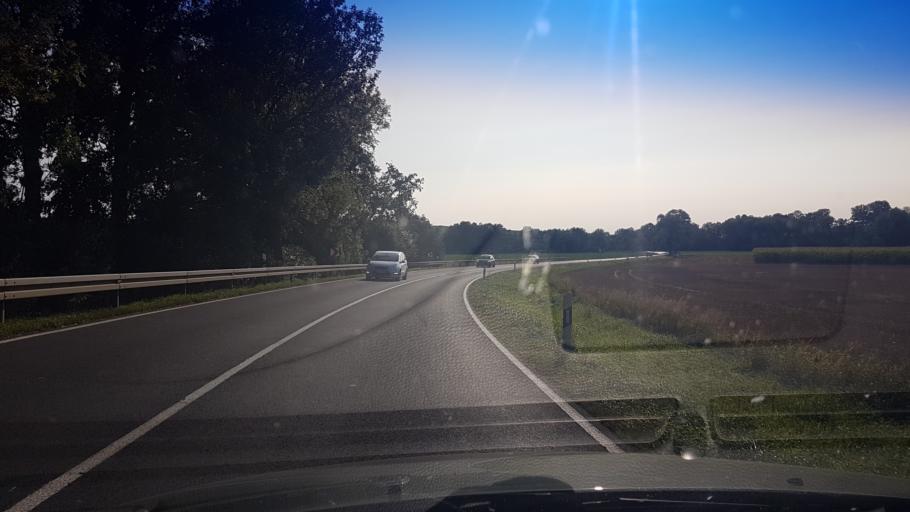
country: DE
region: Bavaria
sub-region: Upper Franconia
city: Memmelsdorf
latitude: 49.9508
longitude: 10.9902
